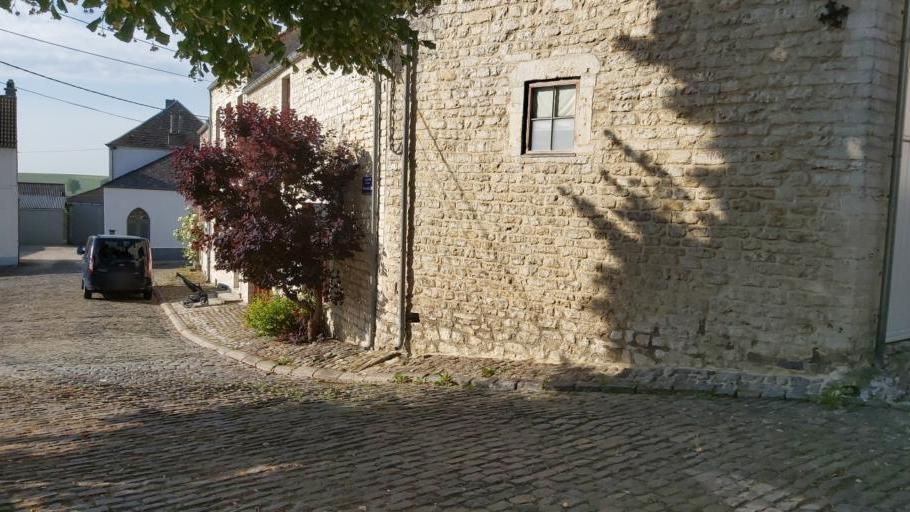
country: BE
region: Wallonia
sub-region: Province du Brabant Wallon
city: Jodoigne
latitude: 50.7468
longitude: 4.8585
